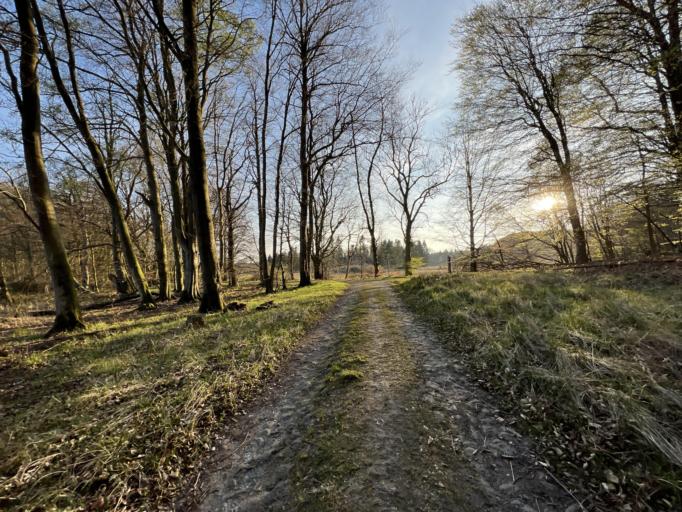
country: DE
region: Mecklenburg-Vorpommern
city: Sassnitz
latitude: 54.5370
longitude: 13.6543
